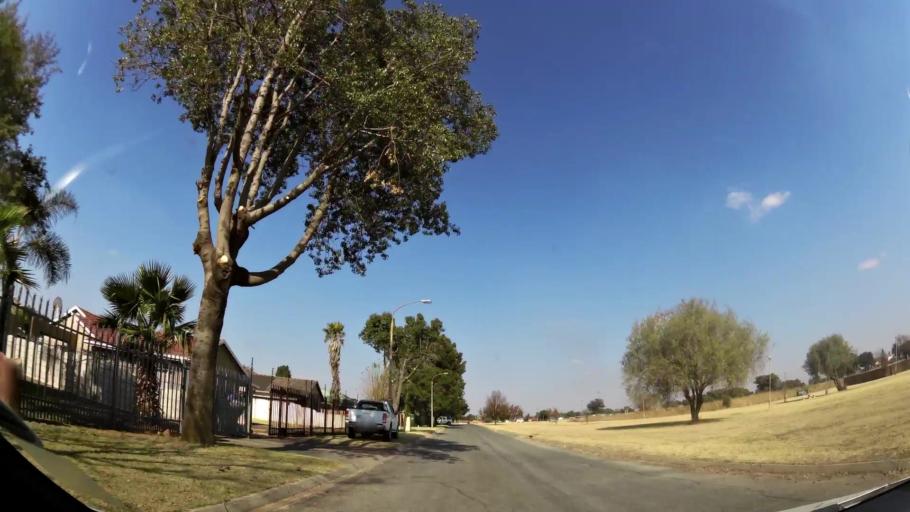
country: ZA
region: Gauteng
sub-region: Ekurhuleni Metropolitan Municipality
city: Boksburg
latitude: -26.2446
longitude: 28.2968
